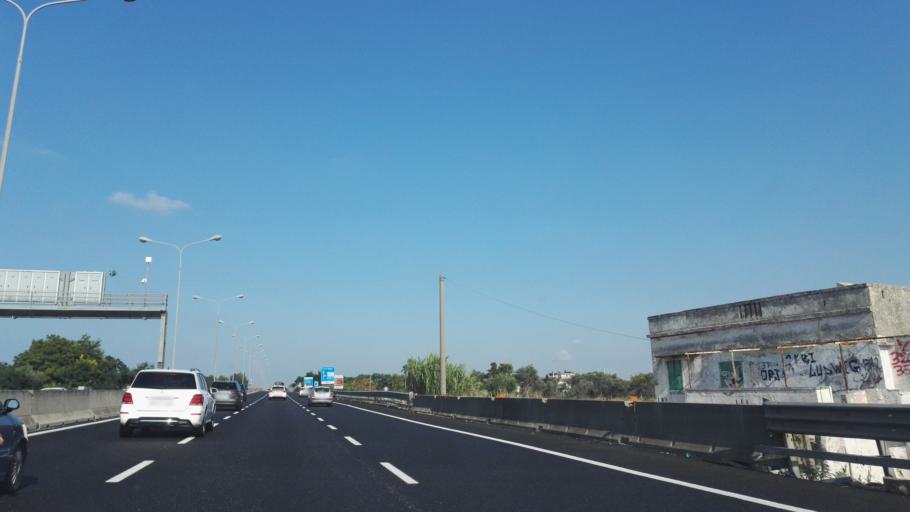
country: IT
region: Apulia
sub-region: Provincia di Bari
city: Bari
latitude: 41.0894
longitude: 16.8788
